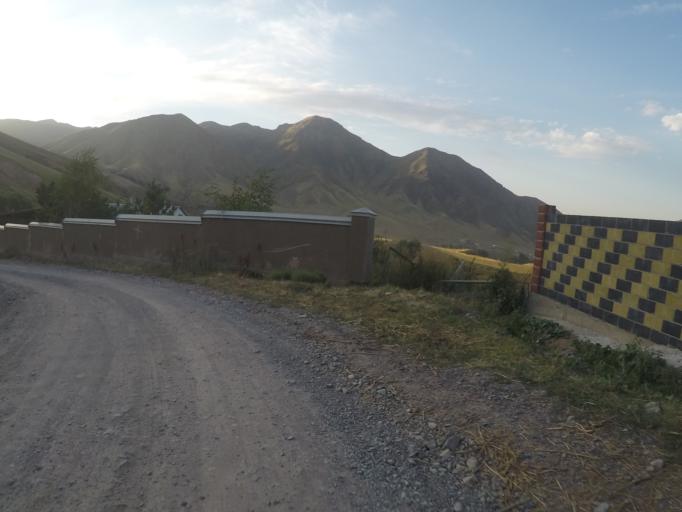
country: KG
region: Chuy
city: Bishkek
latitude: 42.6642
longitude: 74.6500
